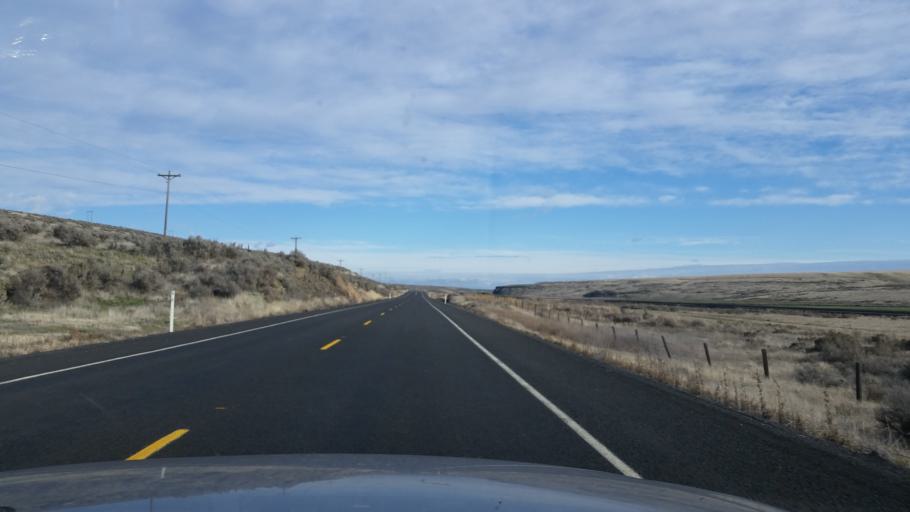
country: US
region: Washington
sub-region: Adams County
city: Ritzville
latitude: 47.3504
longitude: -118.5450
